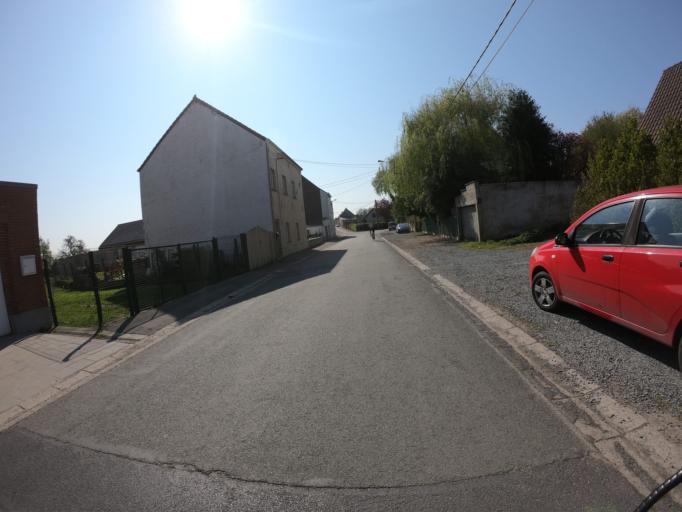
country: BE
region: Wallonia
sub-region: Province du Hainaut
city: Lessines
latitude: 50.7343
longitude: 3.8521
